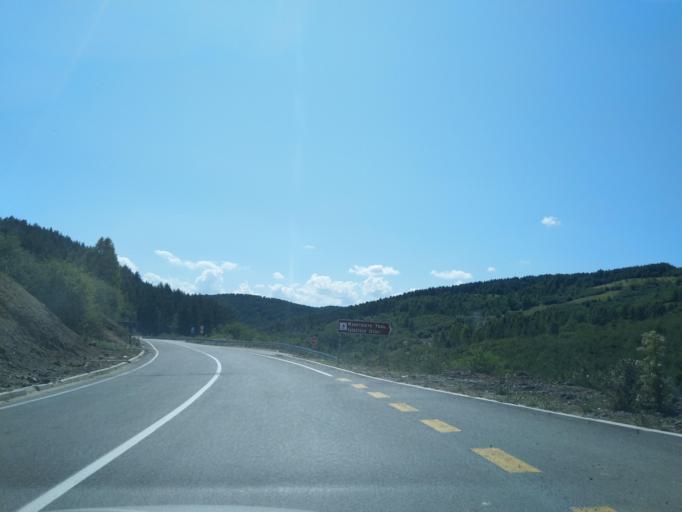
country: RS
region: Central Serbia
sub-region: Zlatiborski Okrug
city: Sjenica
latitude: 43.2869
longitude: 19.9439
